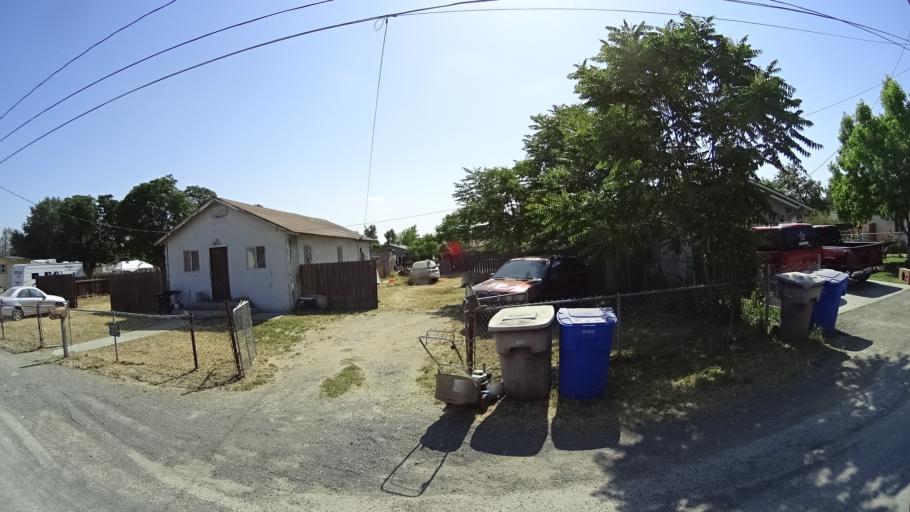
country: US
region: California
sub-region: Kings County
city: Home Garden
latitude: 36.3049
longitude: -119.6340
